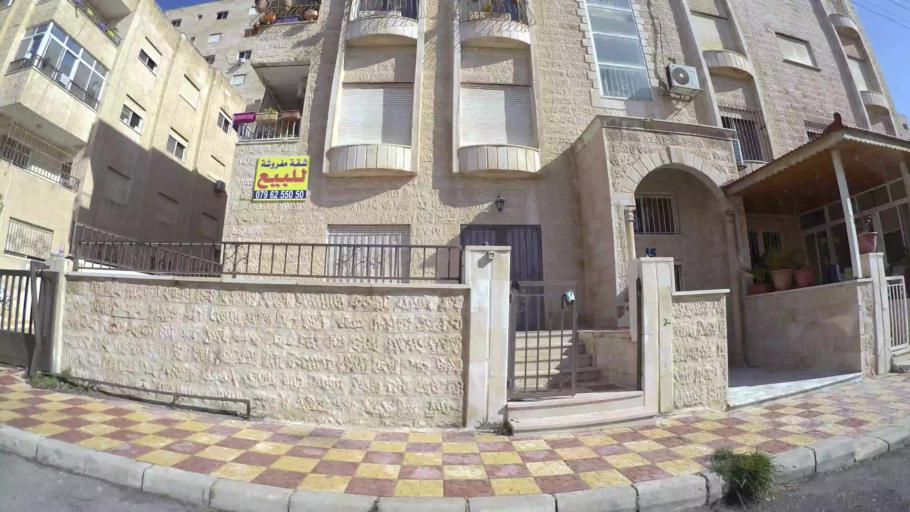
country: JO
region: Amman
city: Al Jubayhah
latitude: 32.0038
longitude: 35.8887
